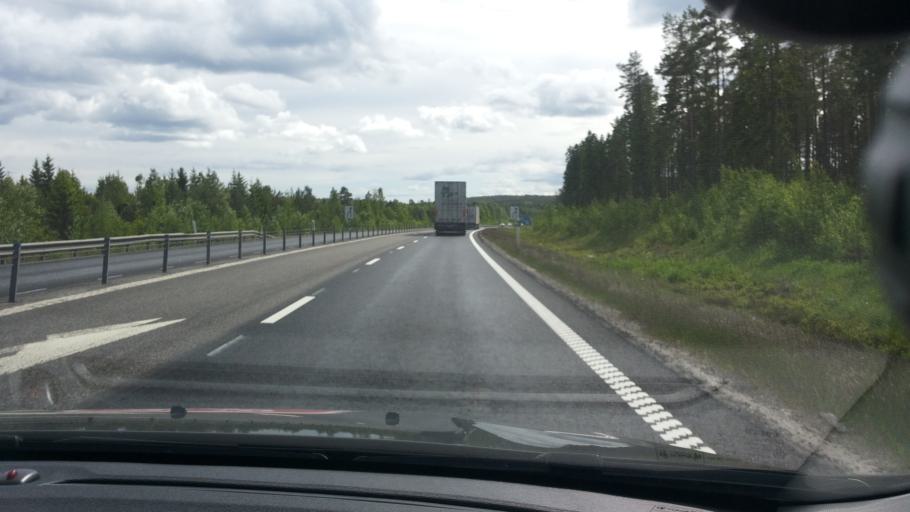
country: SE
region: Vaesternorrland
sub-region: Sundsvalls Kommun
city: Njurundabommen
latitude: 62.2358
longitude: 17.3748
